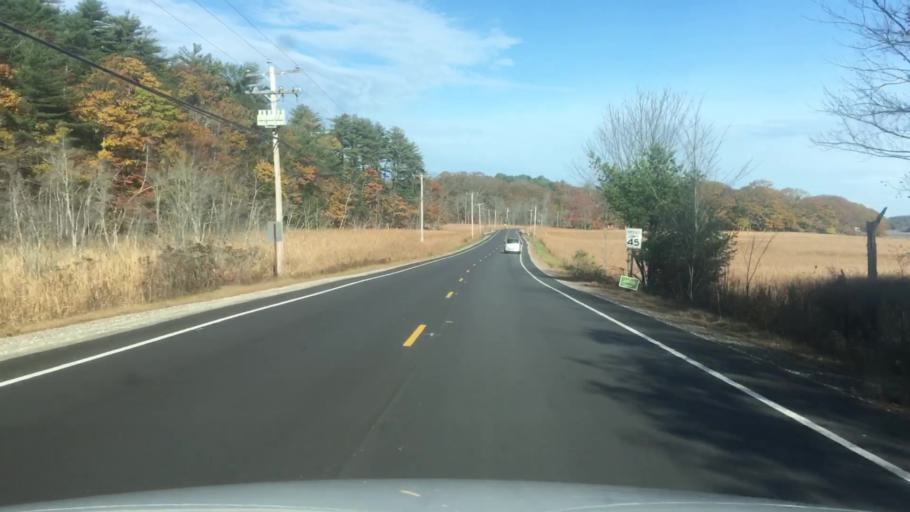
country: US
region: Maine
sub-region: Sagadahoc County
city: Woolwich
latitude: 43.9003
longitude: -69.7962
